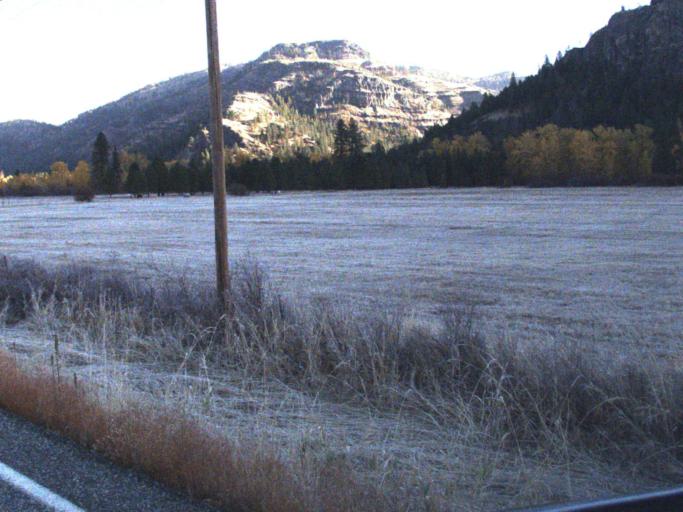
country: US
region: Washington
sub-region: Okanogan County
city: Coulee Dam
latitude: 48.2149
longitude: -118.7093
